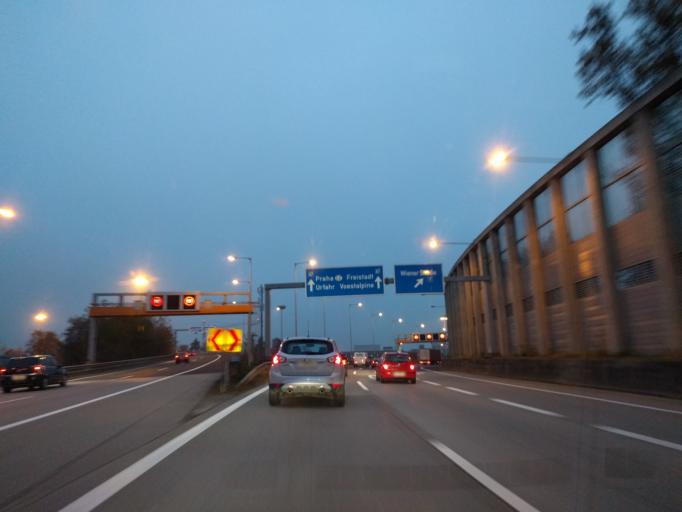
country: AT
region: Upper Austria
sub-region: Linz Stadt
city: Linz
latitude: 48.2672
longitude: 14.2973
